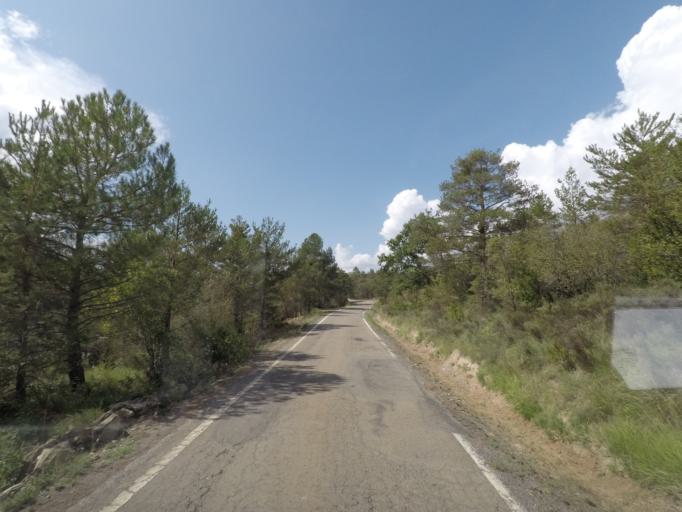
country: ES
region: Aragon
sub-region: Provincia de Huesca
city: Yebra de Basa
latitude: 42.4019
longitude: -0.3578
